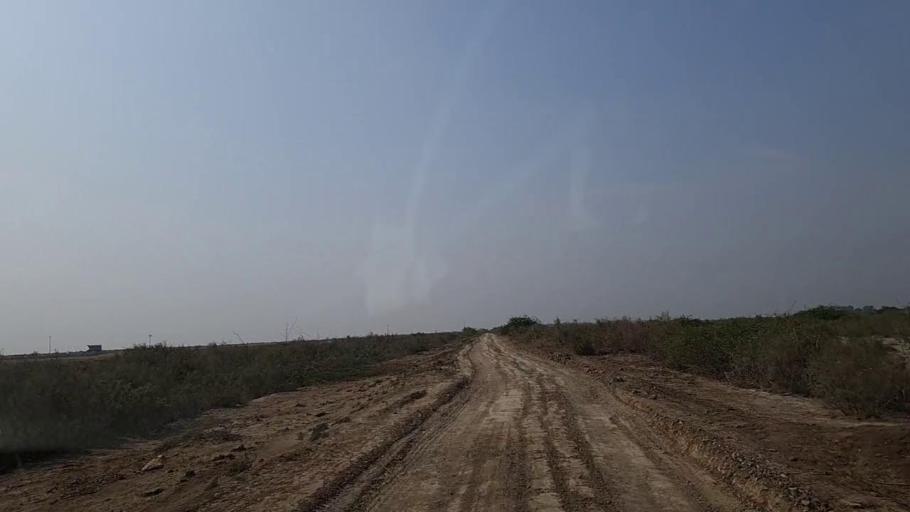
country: PK
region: Sindh
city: Gharo
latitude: 24.6735
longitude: 67.7078
